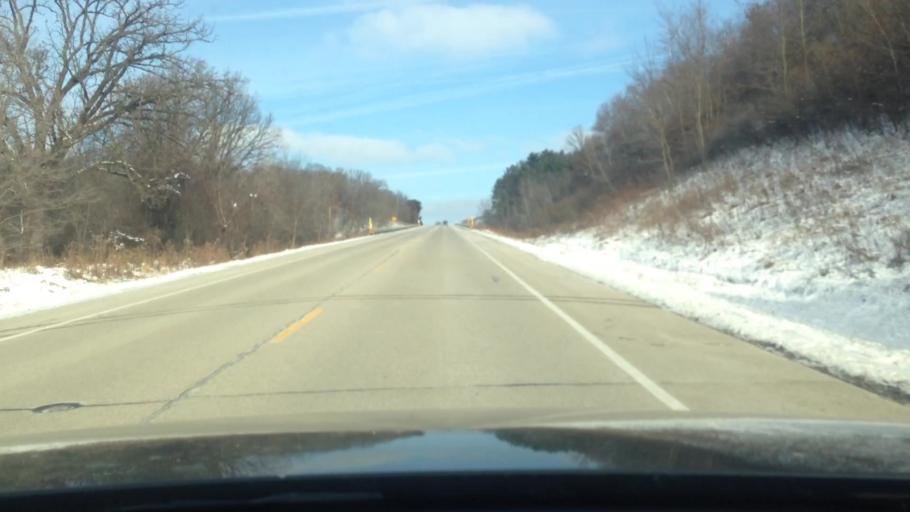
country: US
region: Wisconsin
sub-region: Walworth County
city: East Troy
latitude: 42.7346
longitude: -88.4058
